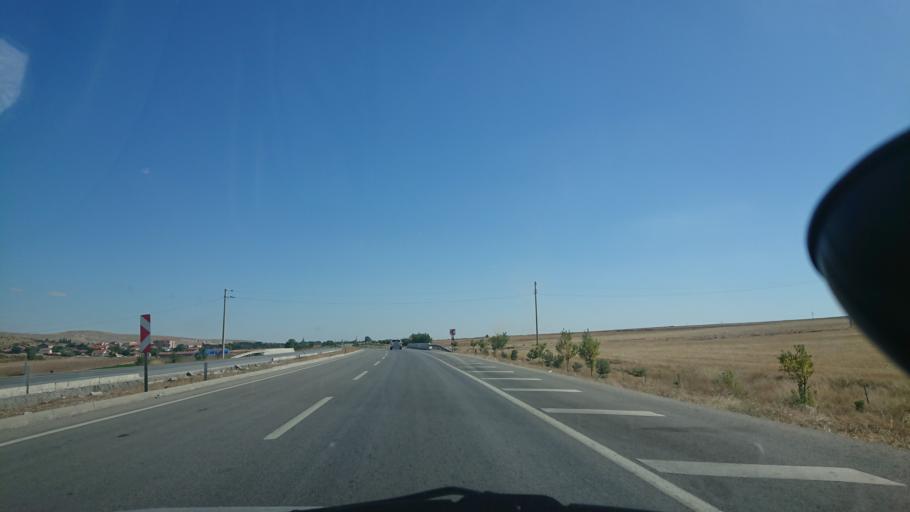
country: TR
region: Eskisehir
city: Mahmudiye
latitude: 39.4975
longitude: 30.9707
